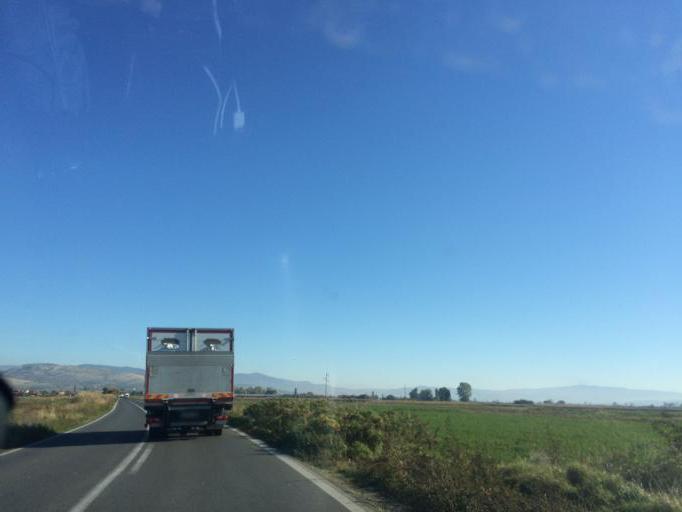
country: MK
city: Obleshevo
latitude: 41.8750
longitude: 22.3219
